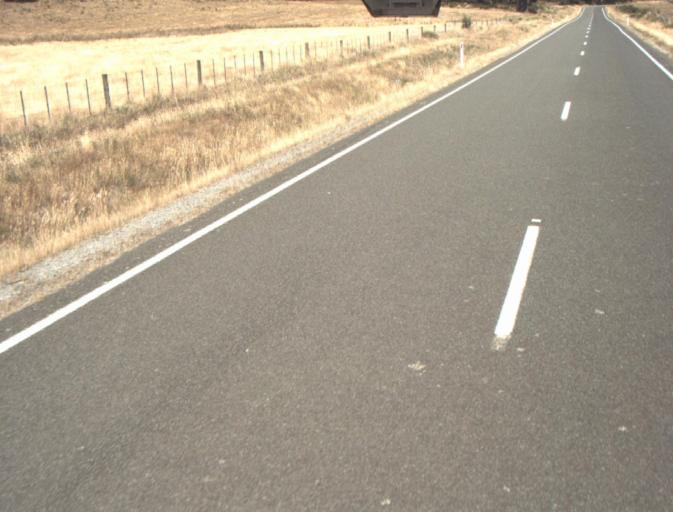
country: AU
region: Tasmania
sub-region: Dorset
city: Scottsdale
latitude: -41.2933
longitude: 147.3854
